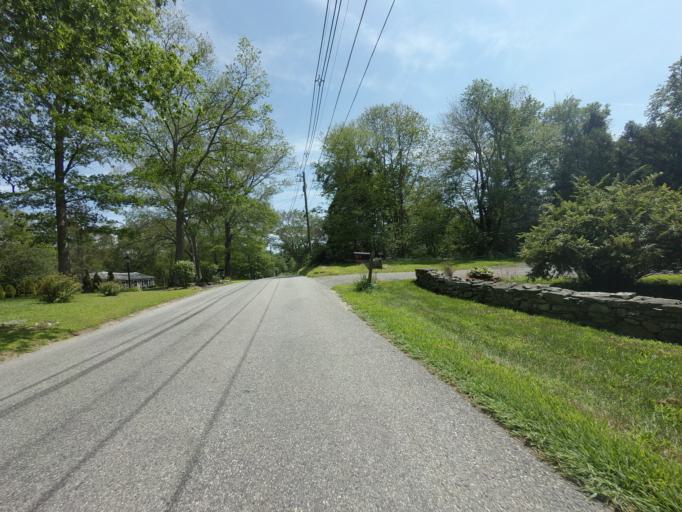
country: US
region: Connecticut
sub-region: Windham County
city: East Brooklyn
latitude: 41.8214
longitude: -71.9286
